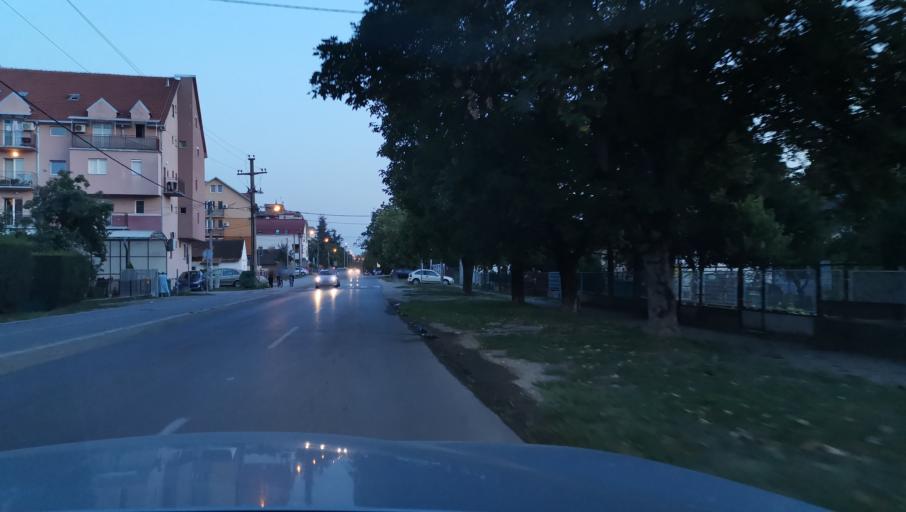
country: RS
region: Central Serbia
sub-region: Belgrade
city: Obrenovac
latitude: 44.6645
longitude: 20.2036
